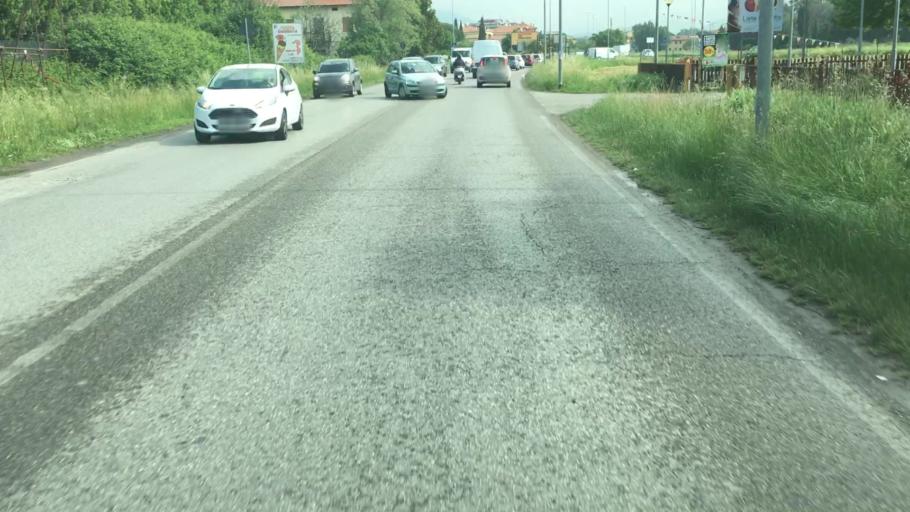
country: IT
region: Tuscany
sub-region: Province of Florence
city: Campi Bisenzio
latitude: 43.8194
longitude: 11.1222
